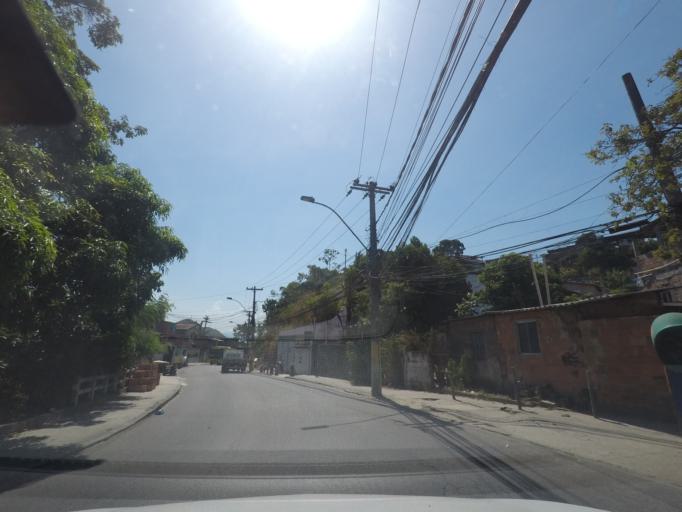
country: BR
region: Rio de Janeiro
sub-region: Niteroi
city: Niteroi
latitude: -22.9052
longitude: -43.0715
